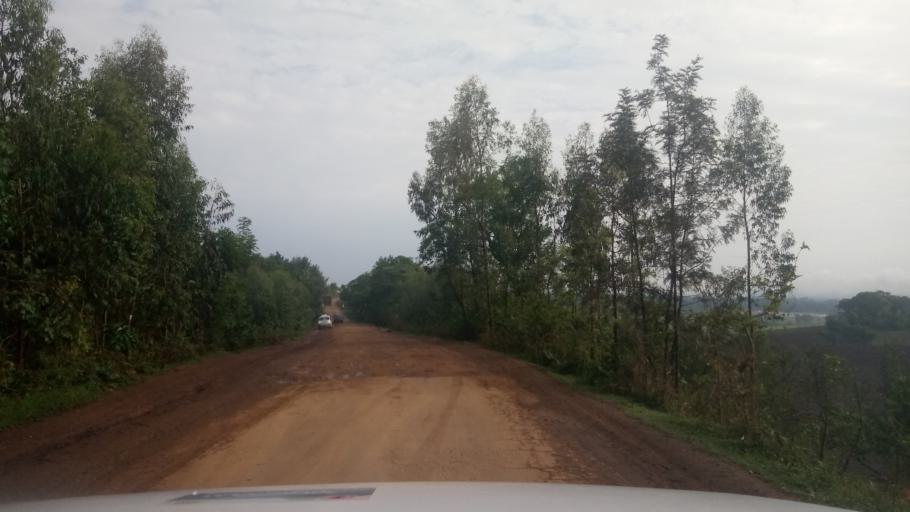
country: ET
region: Oromiya
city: Agaro
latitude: 7.8476
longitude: 36.6570
